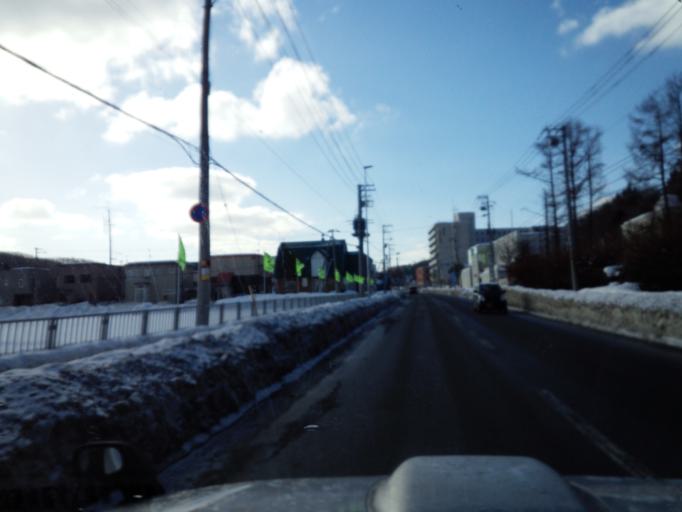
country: JP
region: Hokkaido
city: Sapporo
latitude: 42.9578
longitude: 141.3438
